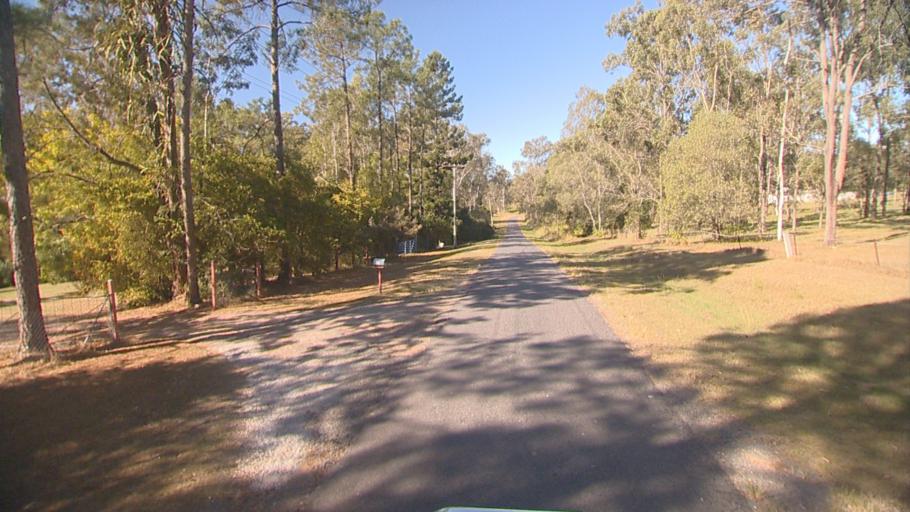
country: AU
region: Queensland
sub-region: Logan
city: North Maclean
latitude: -27.7641
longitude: 153.0271
